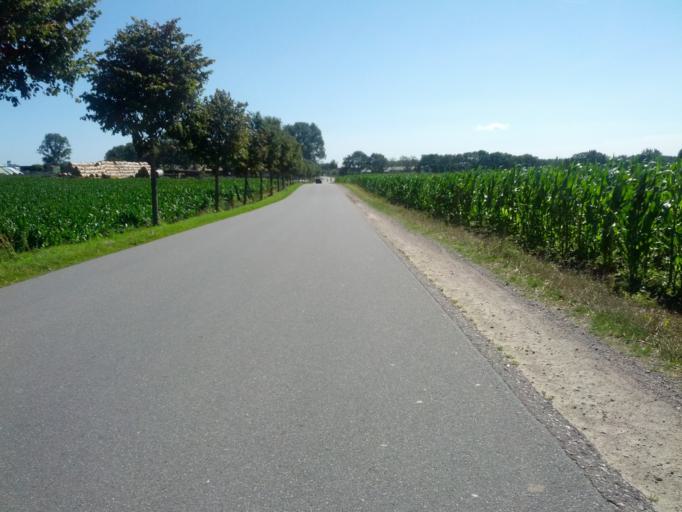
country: DE
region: Mecklenburg-Vorpommern
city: Bastorf
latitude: 54.1279
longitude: 11.6858
